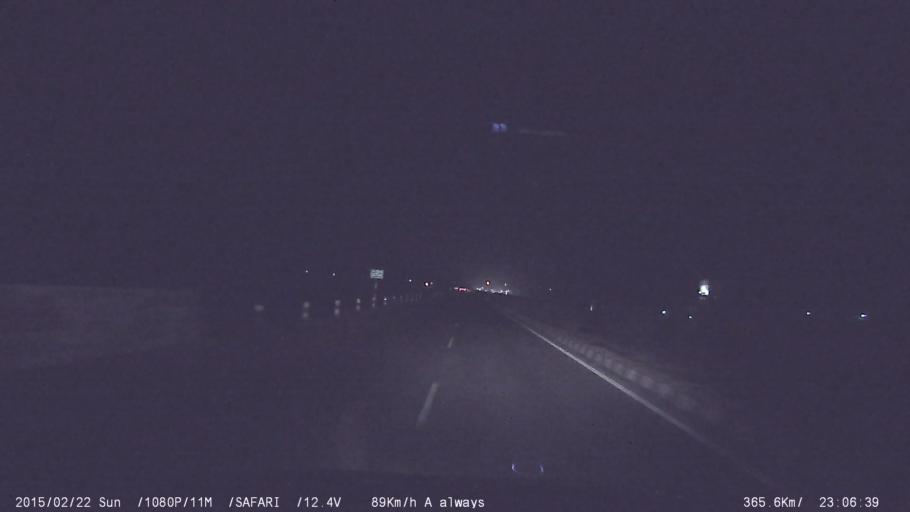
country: IN
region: Tamil Nadu
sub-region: Namakkal
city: Rasipuram
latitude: 11.4298
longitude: 78.1557
